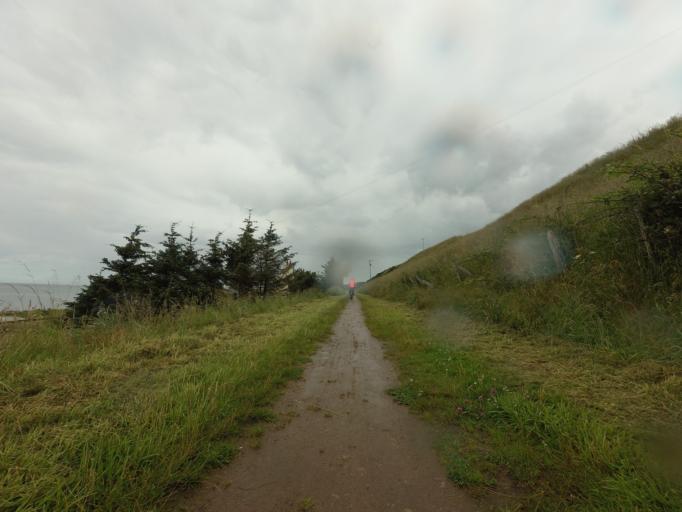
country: GB
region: Scotland
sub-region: Moray
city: Buckie
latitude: 57.6666
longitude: -3.0027
